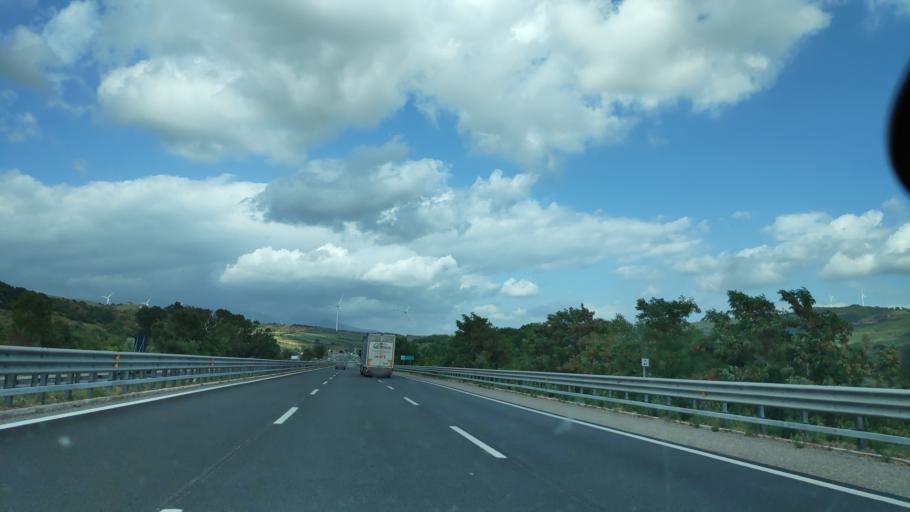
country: IT
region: Campania
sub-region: Provincia di Salerno
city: Serre
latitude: 40.6139
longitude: 15.1522
